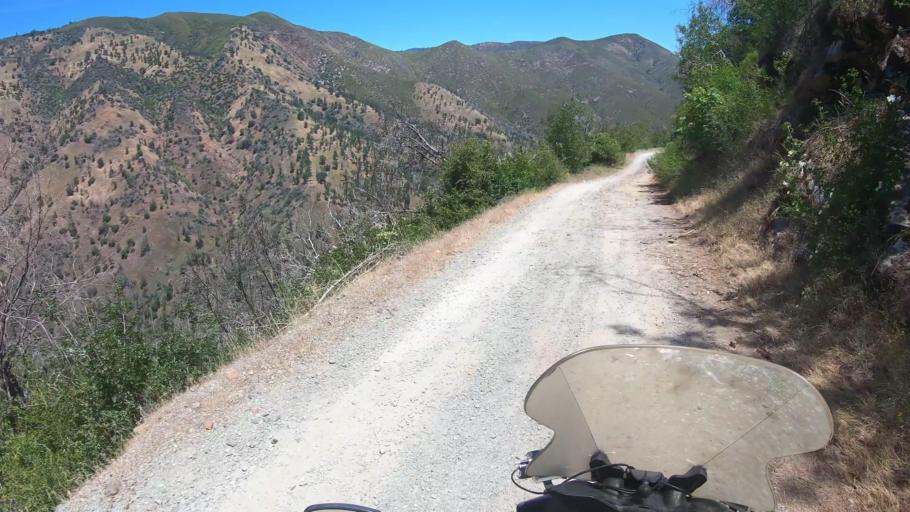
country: US
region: California
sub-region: Tuolumne County
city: Tuolumne City
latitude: 37.8342
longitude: -120.0894
